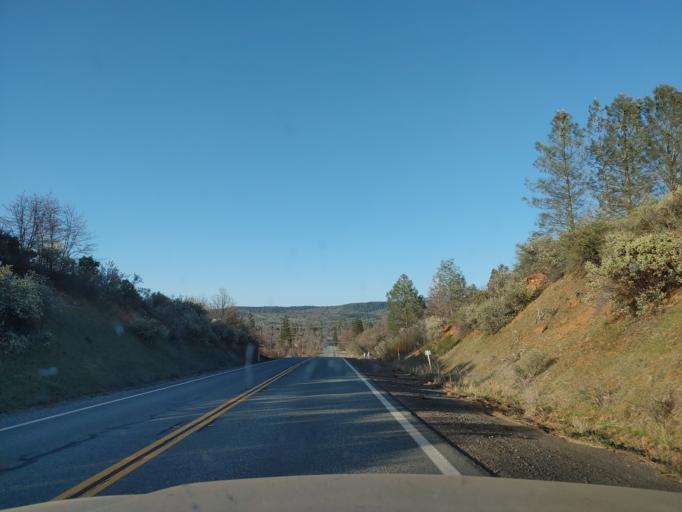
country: US
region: California
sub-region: Shasta County
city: Burney
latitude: 40.8176
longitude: -121.9359
